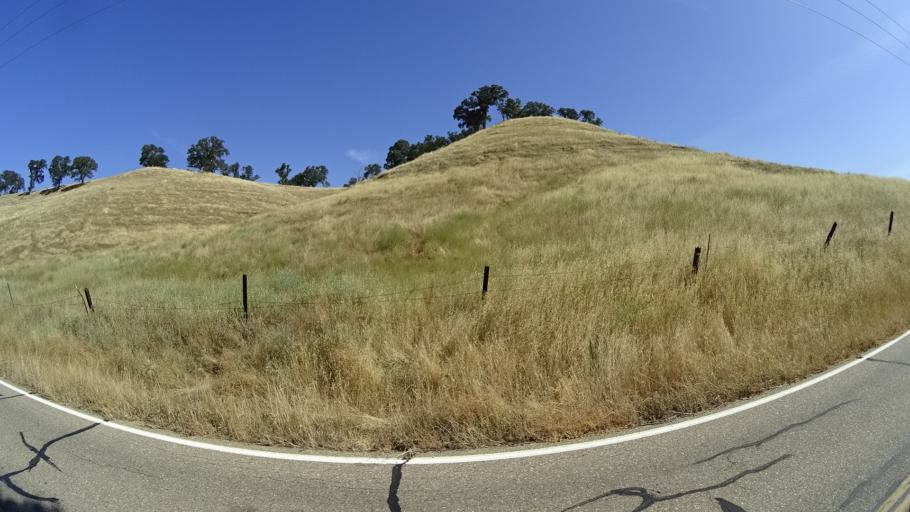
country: US
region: California
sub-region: Calaveras County
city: Rancho Calaveras
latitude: 38.0990
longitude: -120.8817
